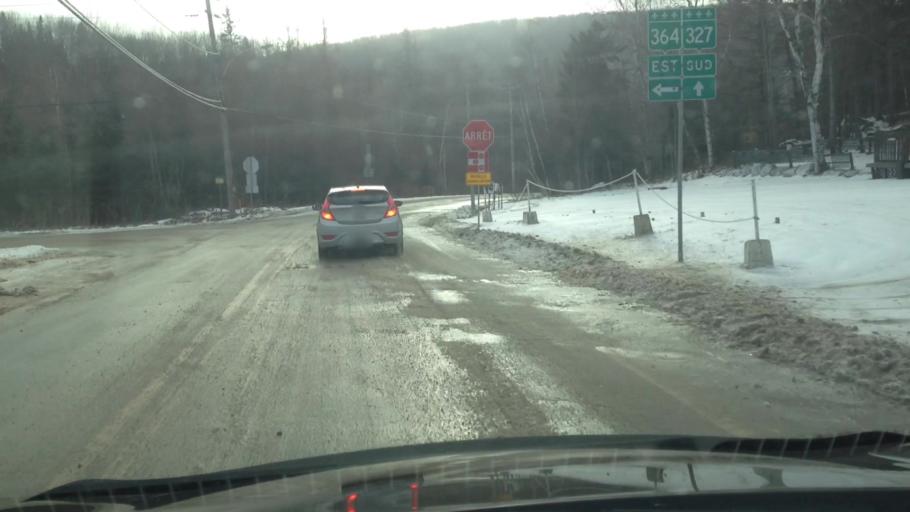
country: CA
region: Quebec
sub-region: Laurentides
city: Mont-Tremblant
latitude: 45.9408
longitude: -74.5473
